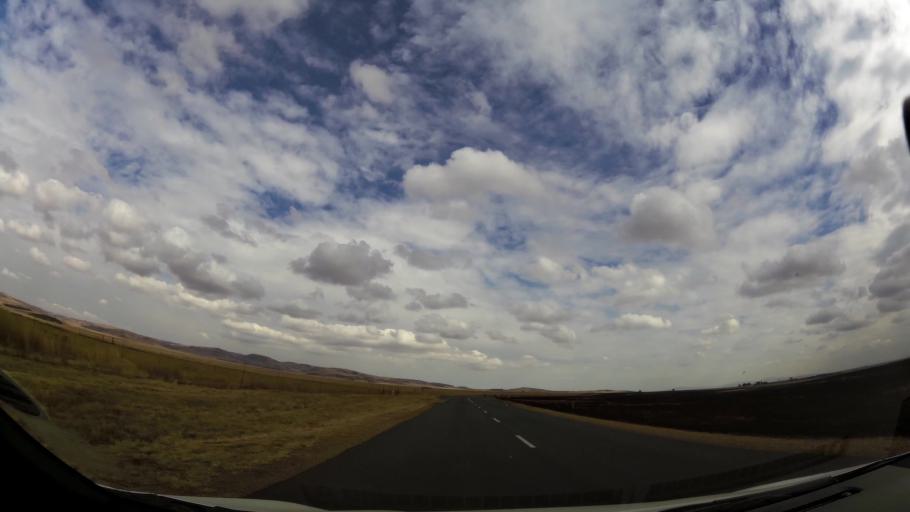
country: ZA
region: Gauteng
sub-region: Sedibeng District Municipality
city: Heidelberg
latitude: -26.4344
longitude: 28.2523
